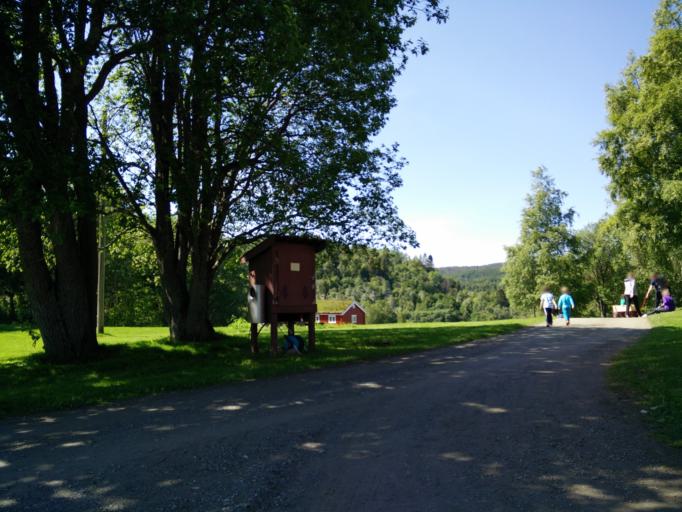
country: NO
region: Sor-Trondelag
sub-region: Trondheim
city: Trondheim
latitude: 63.4202
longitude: 10.3602
